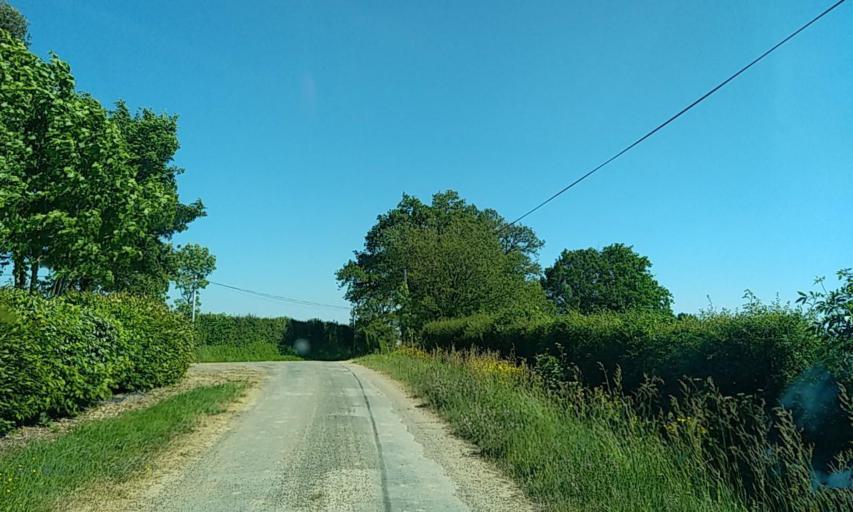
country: FR
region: Poitou-Charentes
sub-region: Departement des Deux-Sevres
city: Boisme
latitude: 46.7921
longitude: -0.4653
